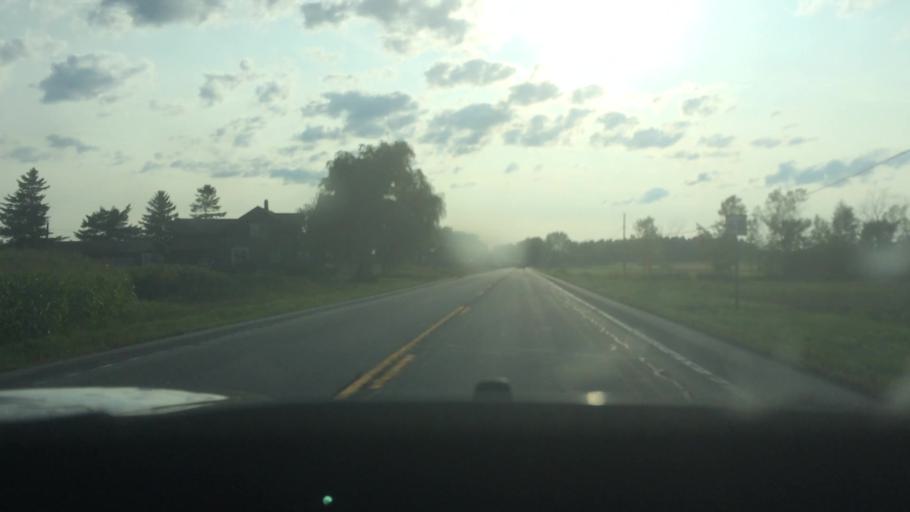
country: US
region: New York
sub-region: St. Lawrence County
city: Ogdensburg
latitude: 44.6746
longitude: -75.4081
